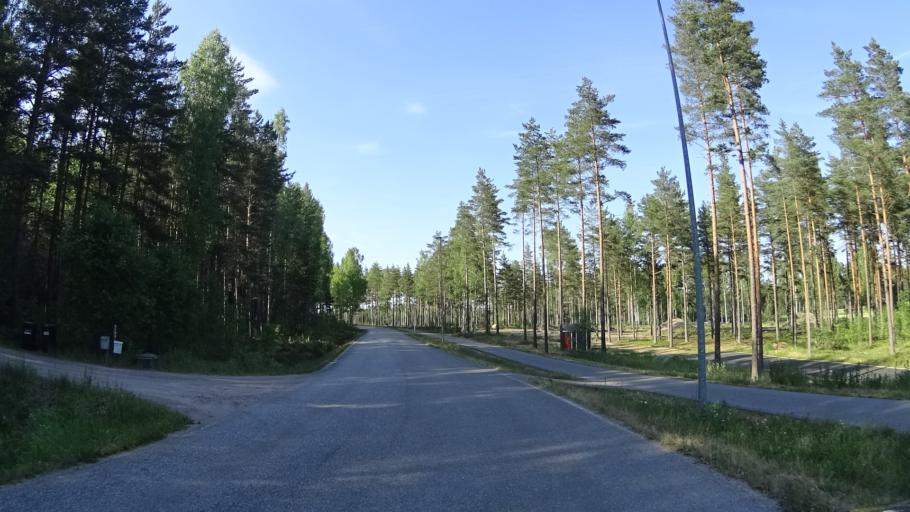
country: FI
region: Uusimaa
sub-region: Helsinki
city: Siuntio
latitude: 60.0843
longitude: 24.3013
